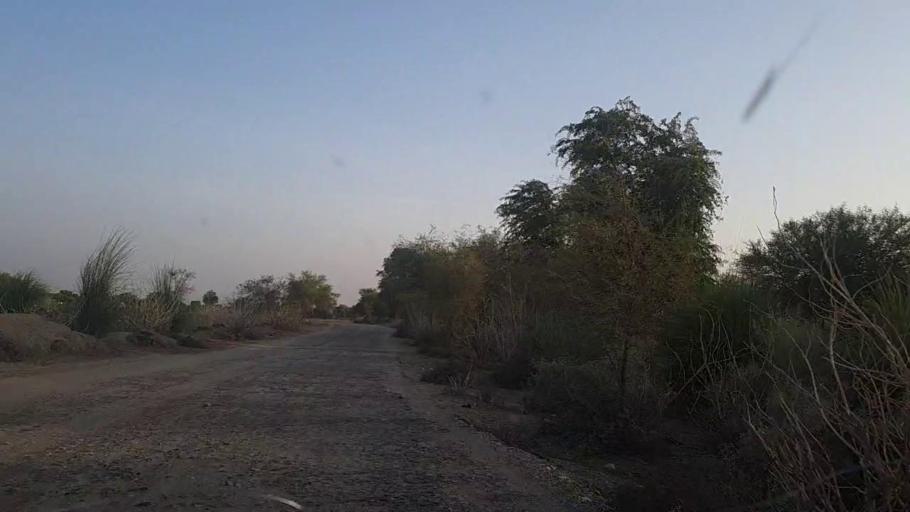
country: PK
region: Sindh
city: Khanpur
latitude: 27.6125
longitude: 69.4382
